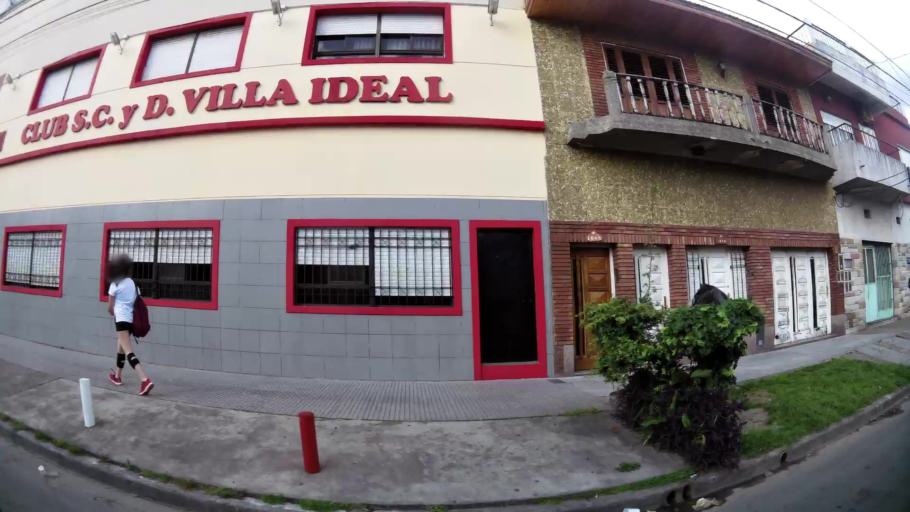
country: AR
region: Buenos Aires
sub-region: Partido de Avellaneda
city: Avellaneda
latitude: -34.6912
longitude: -58.3654
